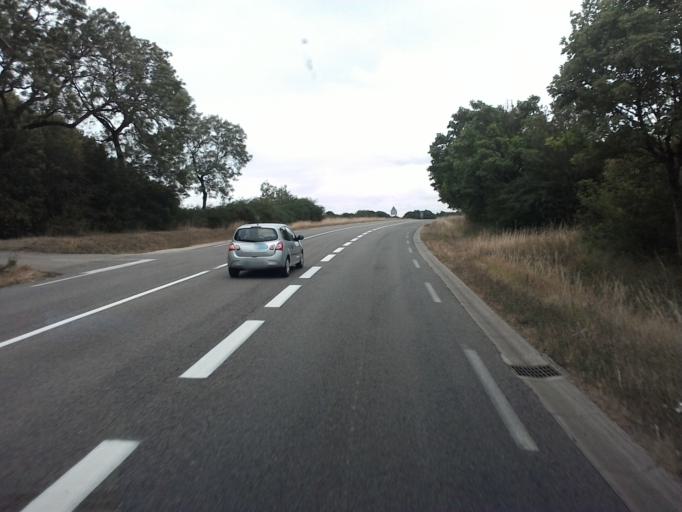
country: FR
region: Lorraine
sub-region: Departement de Meurthe-et-Moselle
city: Colombey-les-Belles
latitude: 48.5762
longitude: 5.9789
